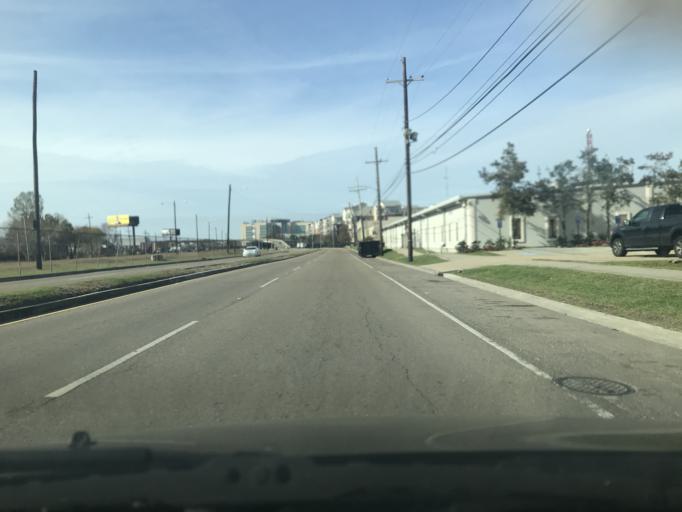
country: US
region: Louisiana
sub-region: Orleans Parish
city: New Orleans
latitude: 29.9564
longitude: -90.0885
